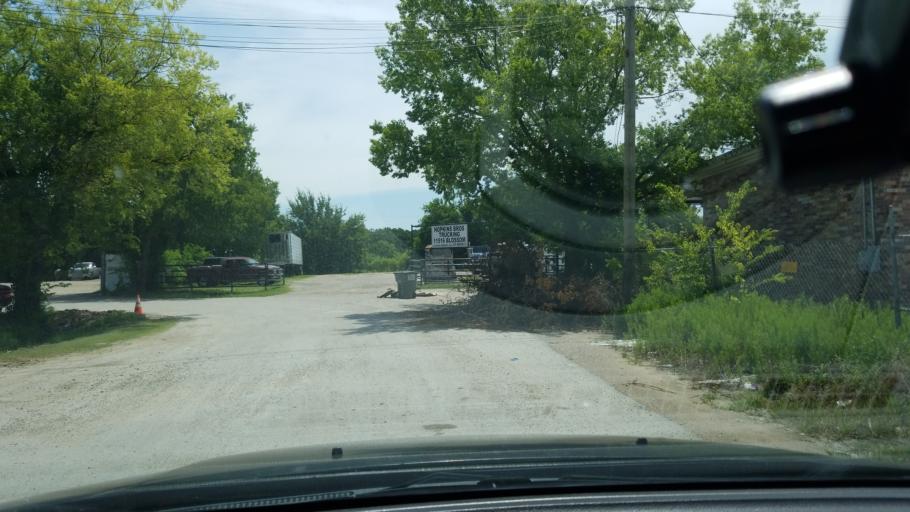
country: US
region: Texas
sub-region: Dallas County
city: Balch Springs
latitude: 32.7436
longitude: -96.6278
